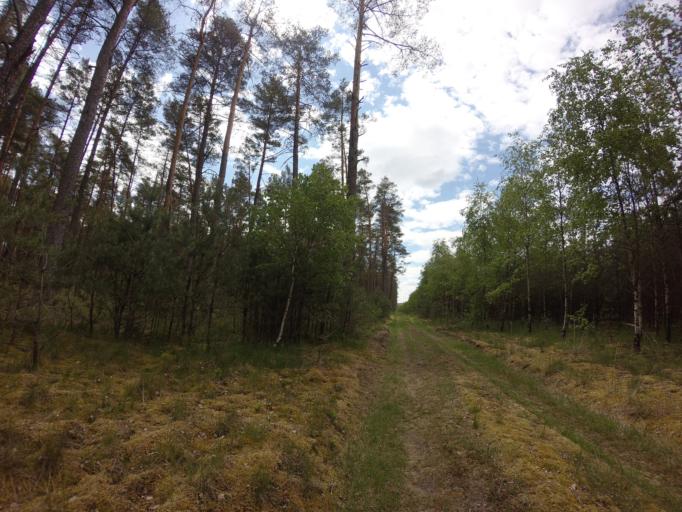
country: PL
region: West Pomeranian Voivodeship
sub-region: Powiat drawski
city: Kalisz Pomorski
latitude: 53.1615
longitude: 15.9701
